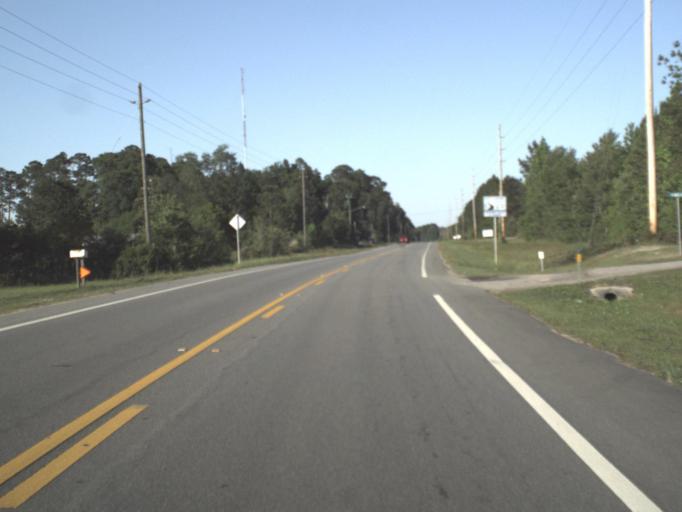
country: US
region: Florida
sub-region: Liberty County
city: Bristol
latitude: 30.3667
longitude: -84.8160
